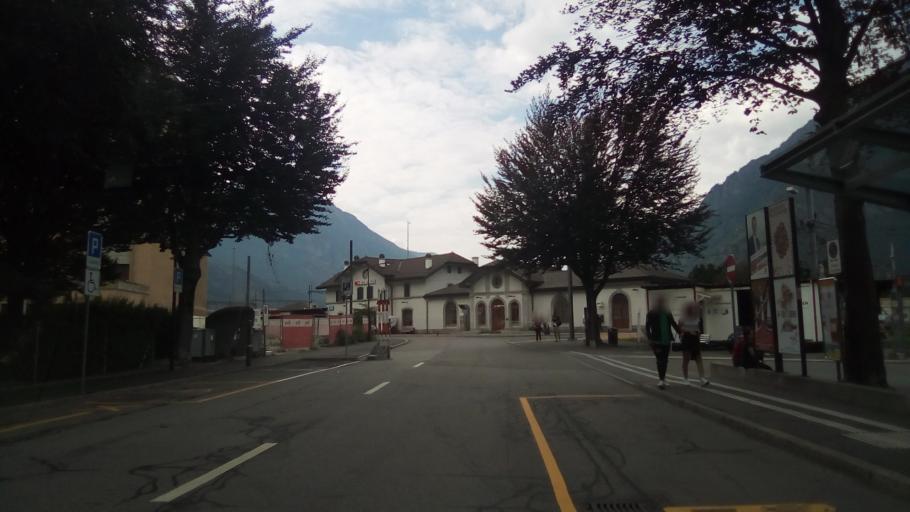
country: CH
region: Valais
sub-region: Martigny District
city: Martigny-Ville
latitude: 46.1052
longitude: 7.0797
